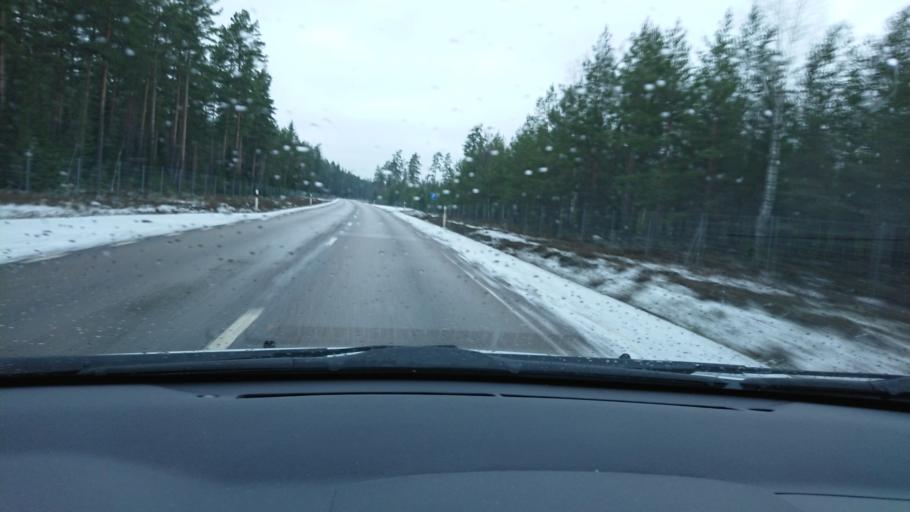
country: SE
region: Kalmar
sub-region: Vimmerby Kommun
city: Vimmerby
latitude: 57.6198
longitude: 15.8434
